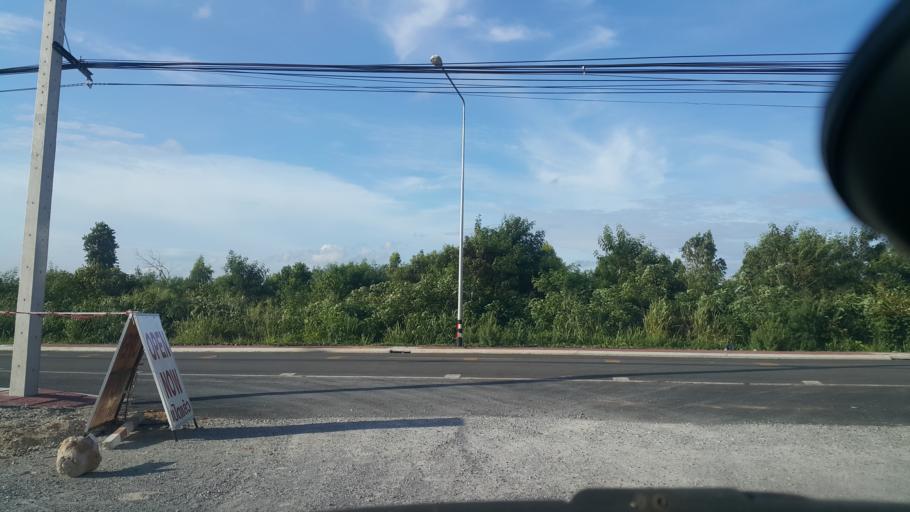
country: TH
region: Rayong
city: Ban Chang
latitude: 12.7717
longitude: 100.9503
